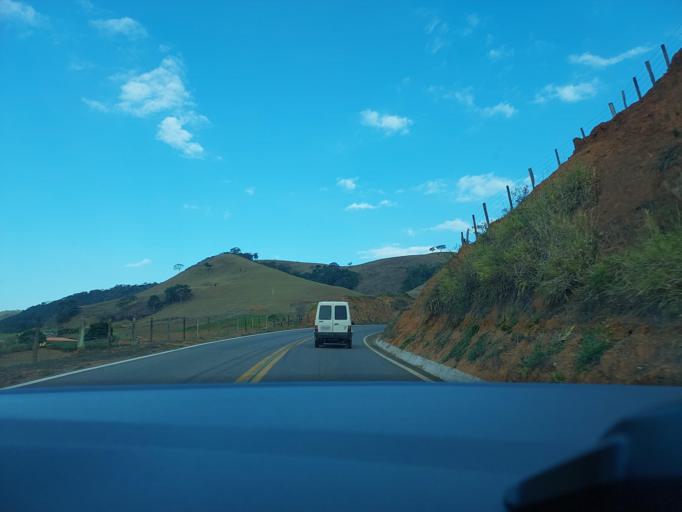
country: BR
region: Minas Gerais
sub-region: Muriae
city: Muriae
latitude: -21.0583
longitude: -42.5016
